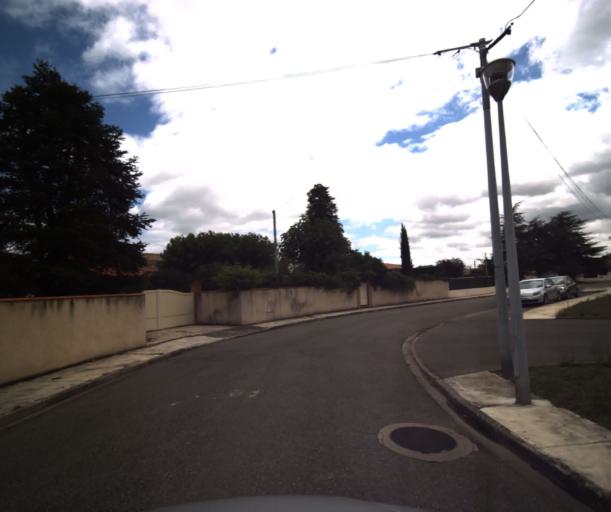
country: FR
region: Midi-Pyrenees
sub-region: Departement de la Haute-Garonne
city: Pinsaguel
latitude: 43.4961
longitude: 1.3842
